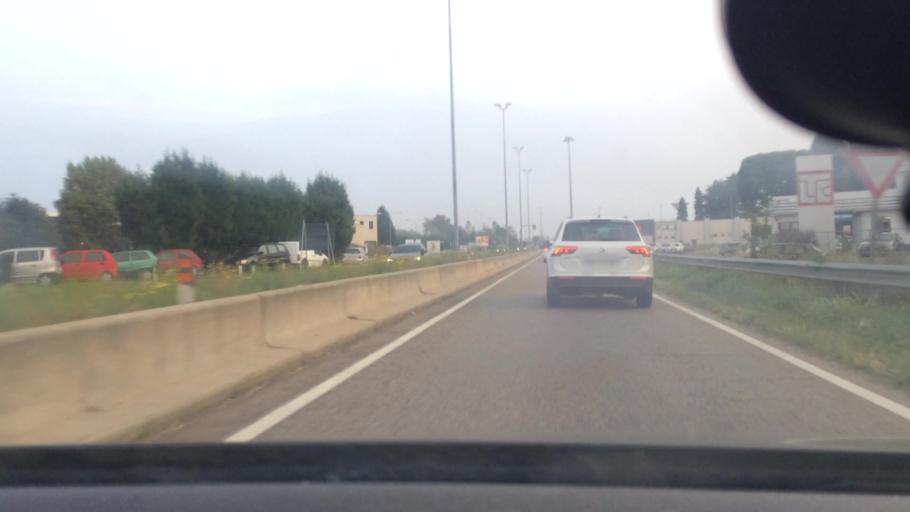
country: IT
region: Lombardy
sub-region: Citta metropolitana di Milano
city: Villa Cortese
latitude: 45.5697
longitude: 8.8994
